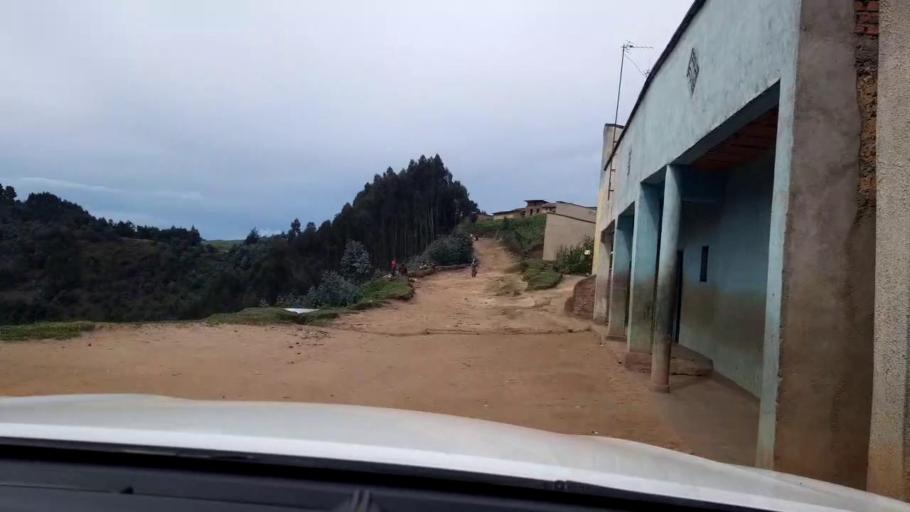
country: RW
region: Western Province
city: Kibuye
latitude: -1.8807
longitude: 29.4546
